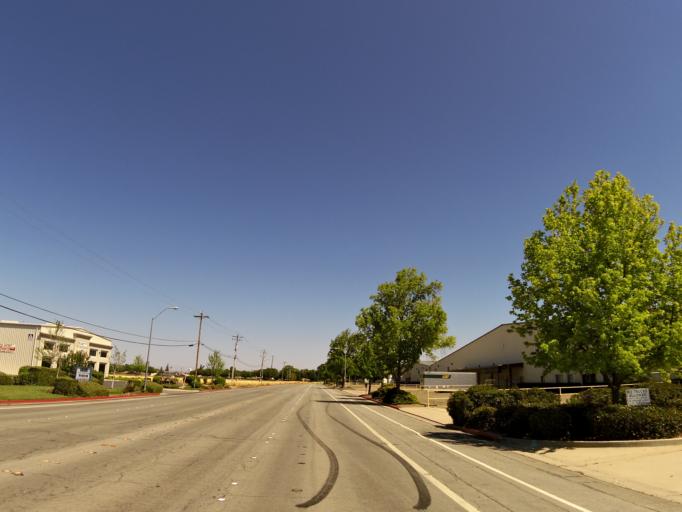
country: US
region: California
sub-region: Merced County
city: Merced
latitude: 37.2917
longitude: -120.5115
